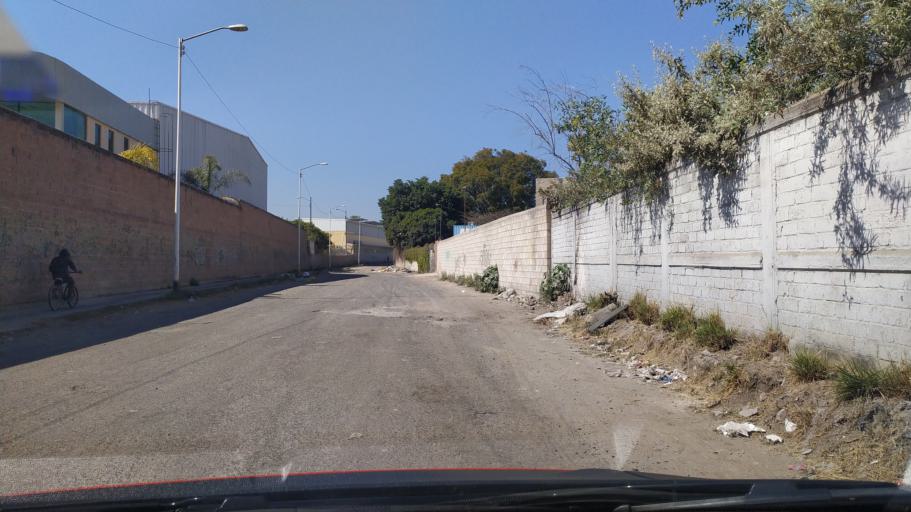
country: MX
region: Jalisco
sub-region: Tlajomulco de Zuniga
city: Palomar
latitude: 20.6278
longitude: -103.4407
